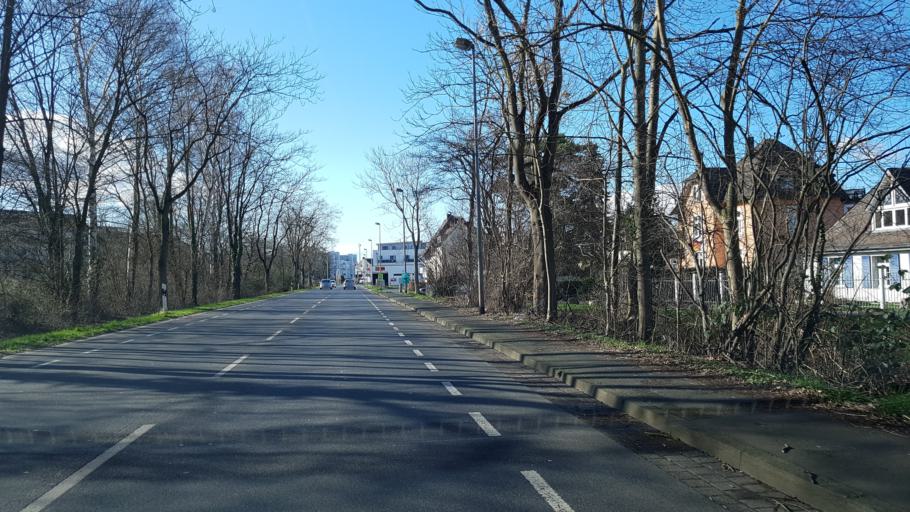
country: DE
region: North Rhine-Westphalia
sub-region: Regierungsbezirk Koln
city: Hennef
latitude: 50.7726
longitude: 7.2948
